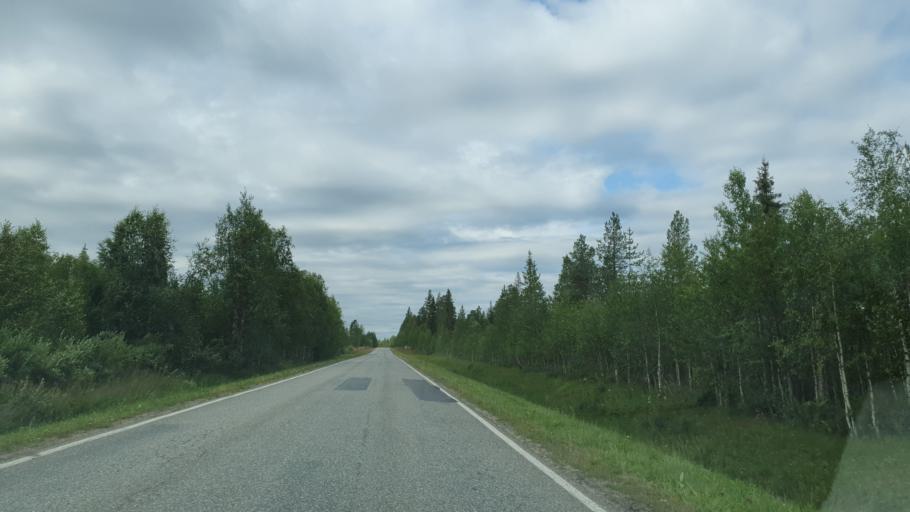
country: FI
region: Lapland
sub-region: Tunturi-Lappi
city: Kittilae
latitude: 67.6157
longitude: 25.3559
